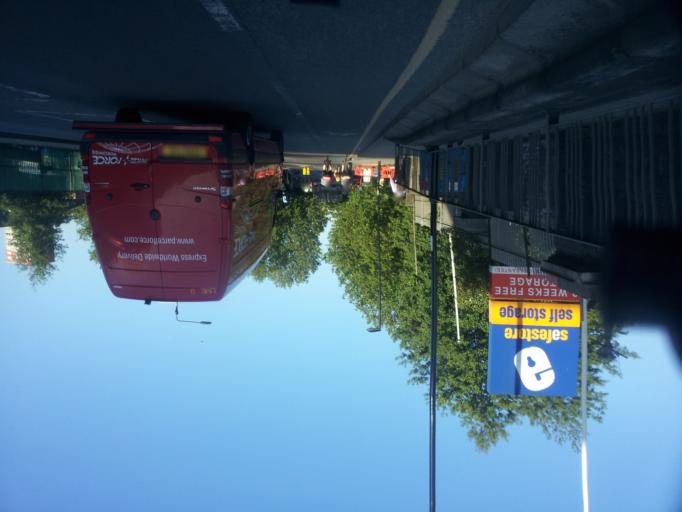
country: GB
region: England
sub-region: Greater London
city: Poplar
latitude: 51.4861
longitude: -0.0354
